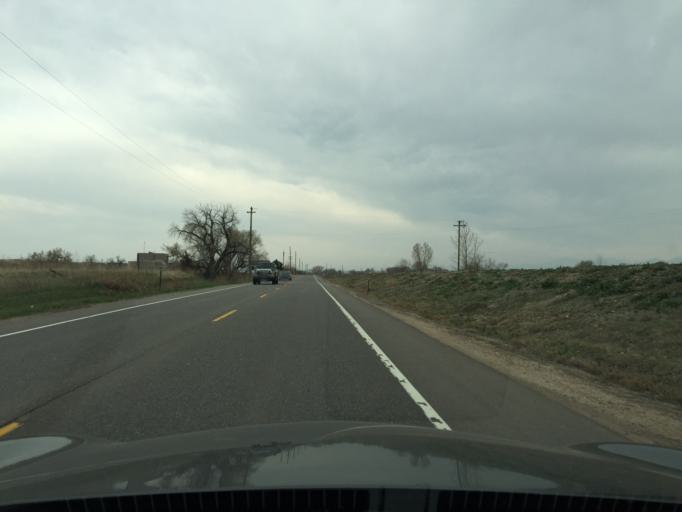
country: US
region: Colorado
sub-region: Boulder County
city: Lafayette
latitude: 40.0056
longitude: -105.0571
